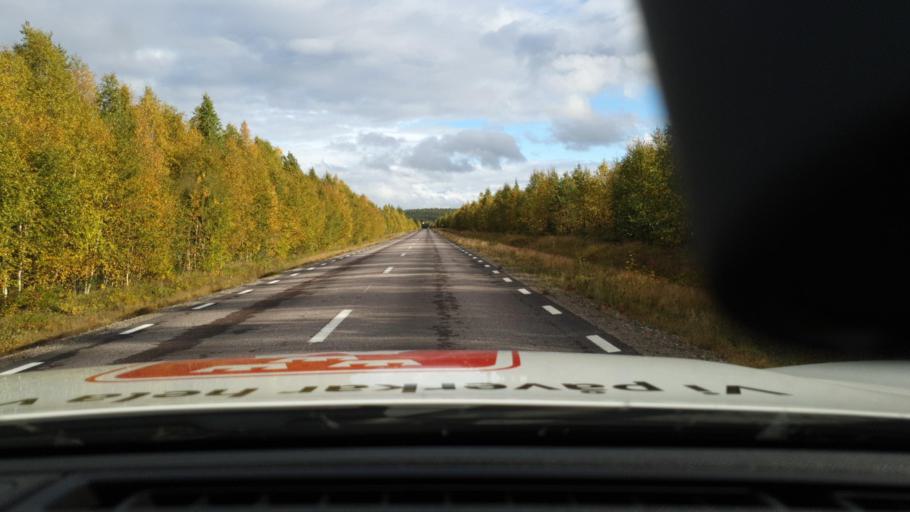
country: SE
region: Norrbotten
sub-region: Overkalix Kommun
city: OEverkalix
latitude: 66.9773
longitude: 22.6286
